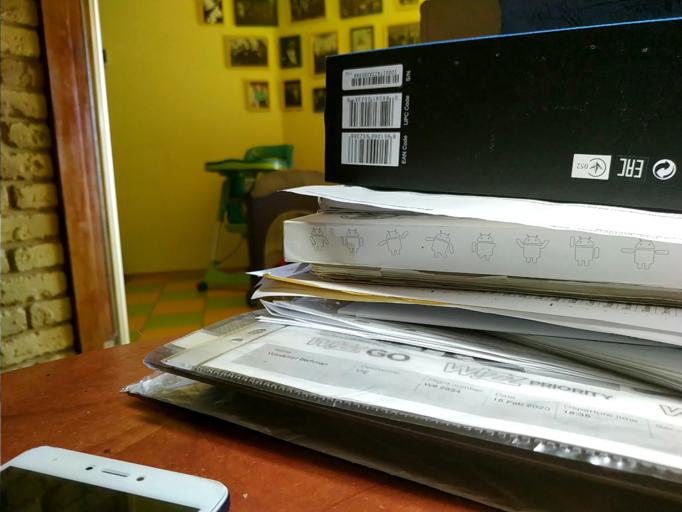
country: RU
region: Novgorod
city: Kholm
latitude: 59.2642
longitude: 32.7982
